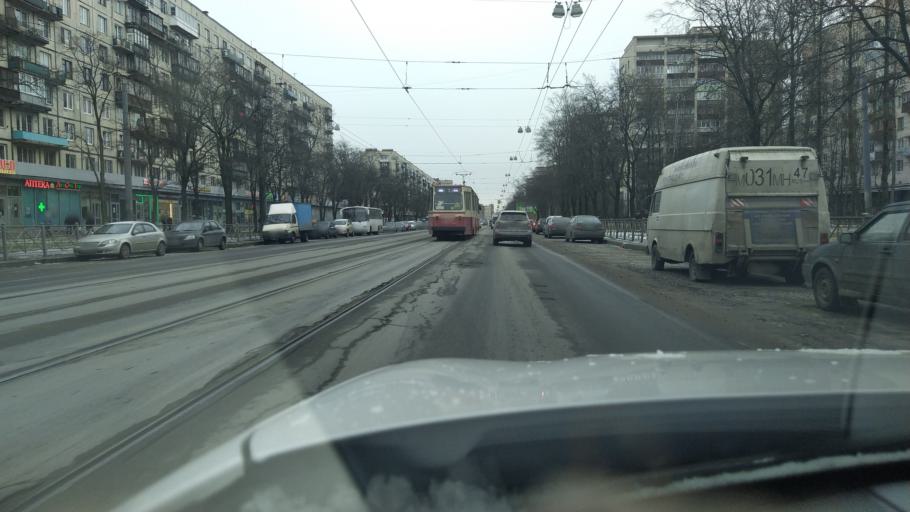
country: RU
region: Leningrad
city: Akademicheskoe
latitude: 60.0094
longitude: 30.4121
